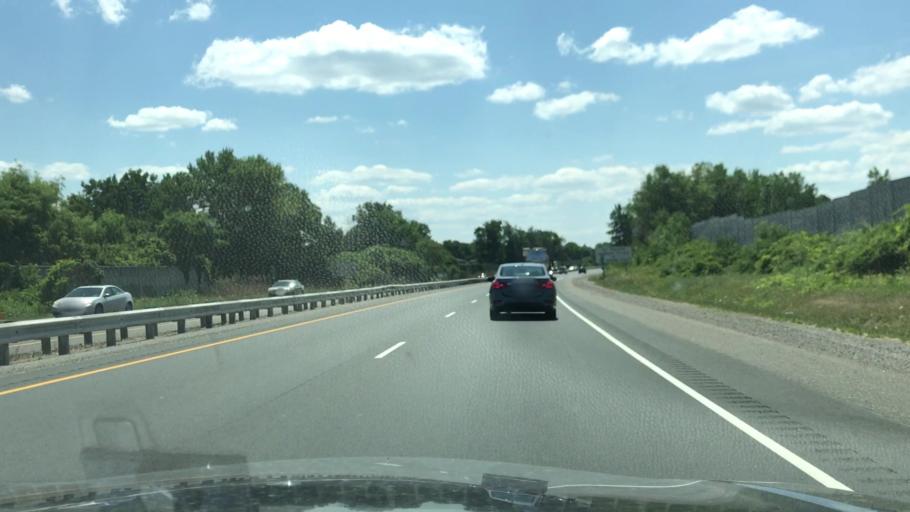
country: CA
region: Ontario
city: Niagara Falls
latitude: 43.1263
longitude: -79.1232
